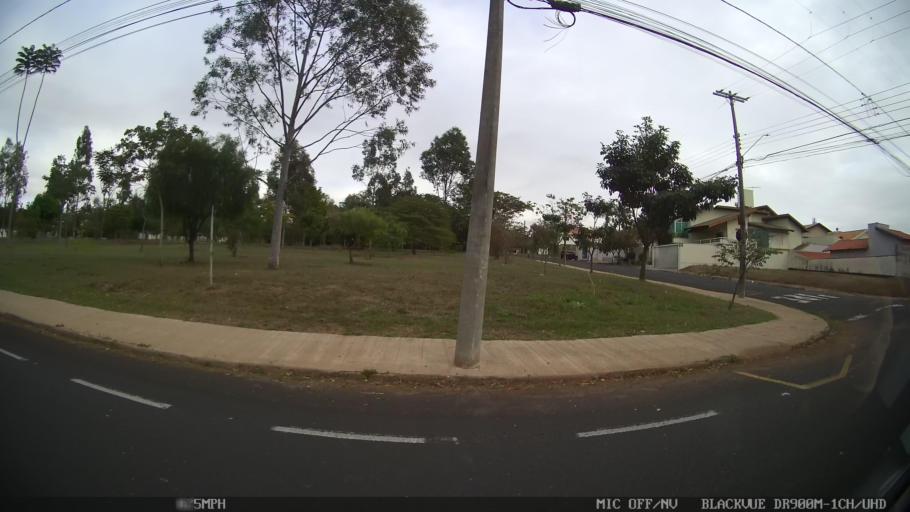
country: BR
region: Sao Paulo
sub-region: Sao Jose Do Rio Preto
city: Sao Jose do Rio Preto
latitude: -20.8366
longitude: -49.3951
